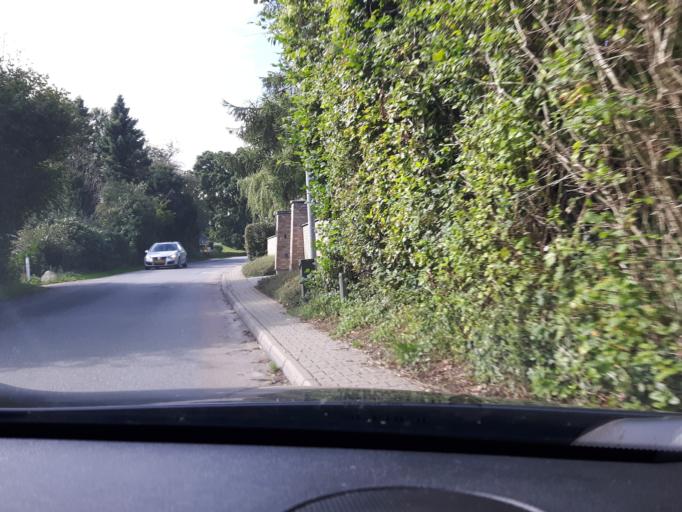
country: DK
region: South Denmark
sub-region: Fredericia Kommune
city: Fredericia
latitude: 55.6238
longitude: 9.7896
